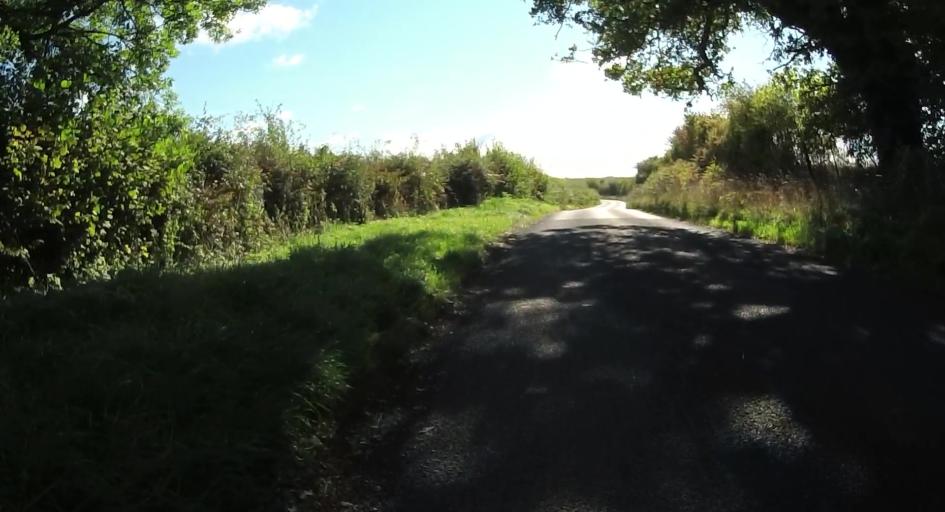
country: GB
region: England
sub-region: Hampshire
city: Hook
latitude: 51.2595
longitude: -0.9910
